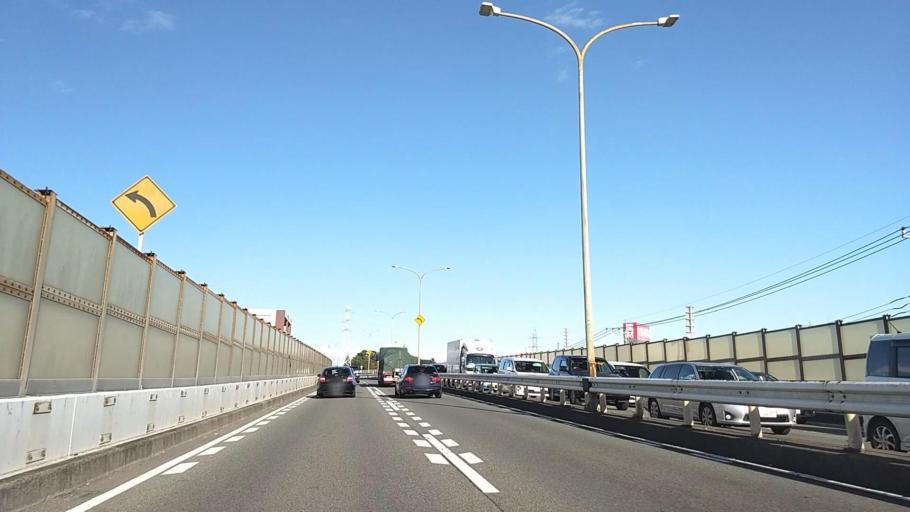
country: JP
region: Tokyo
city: Chofugaoka
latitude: 35.5815
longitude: 139.5954
